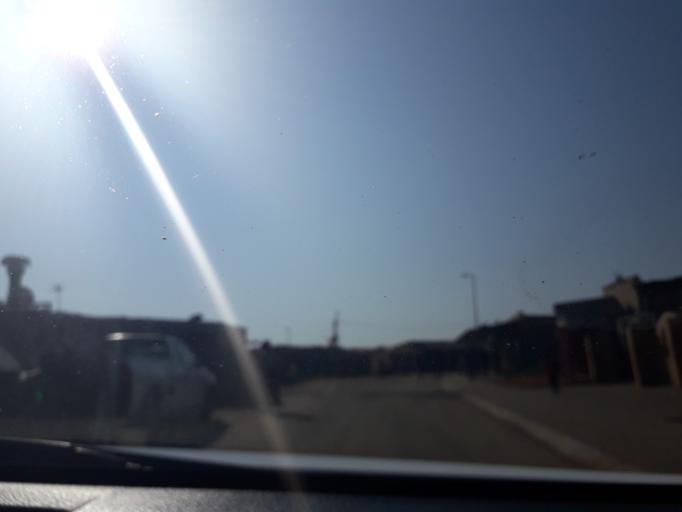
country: ZA
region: Gauteng
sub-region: Ekurhuleni Metropolitan Municipality
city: Tembisa
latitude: -25.9958
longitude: 28.2016
